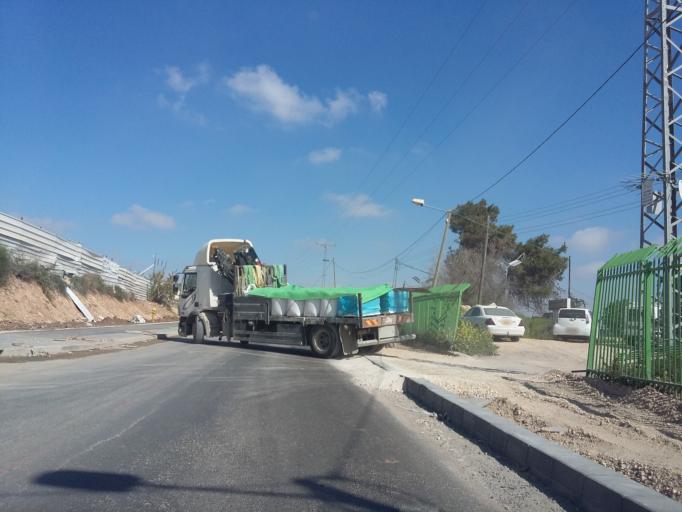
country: PS
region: West Bank
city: Ar Ram wa Dahiyat al Barid
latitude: 31.8545
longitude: 35.2239
